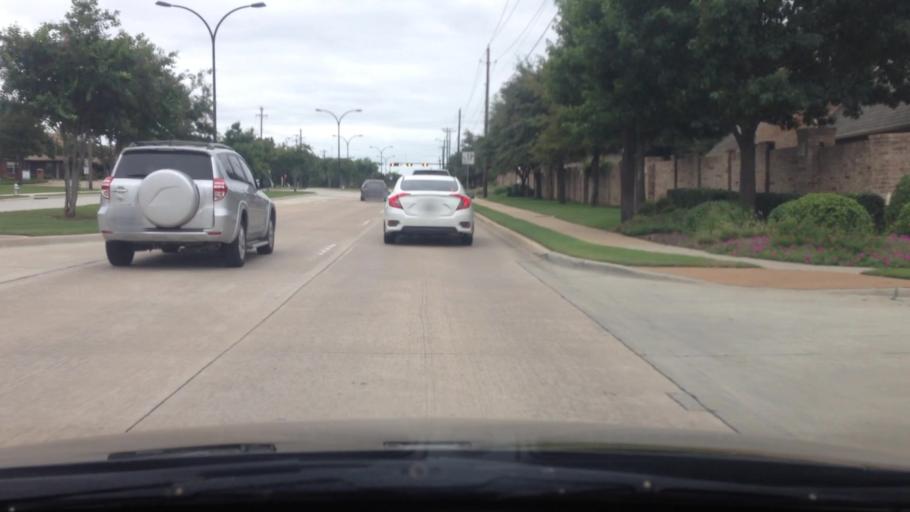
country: US
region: Texas
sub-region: Tarrant County
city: Keller
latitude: 32.9139
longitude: -97.2323
